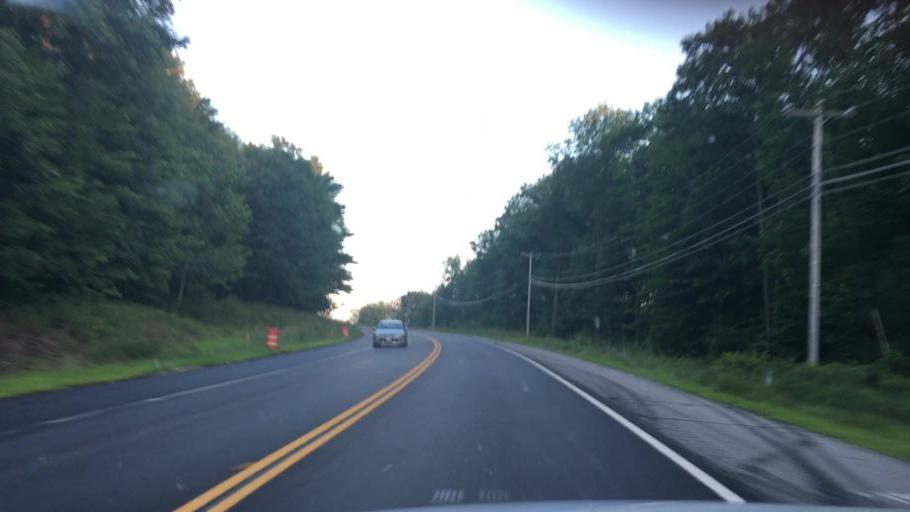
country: US
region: Maine
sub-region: Androscoggin County
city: Turner
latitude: 44.2650
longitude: -70.2659
